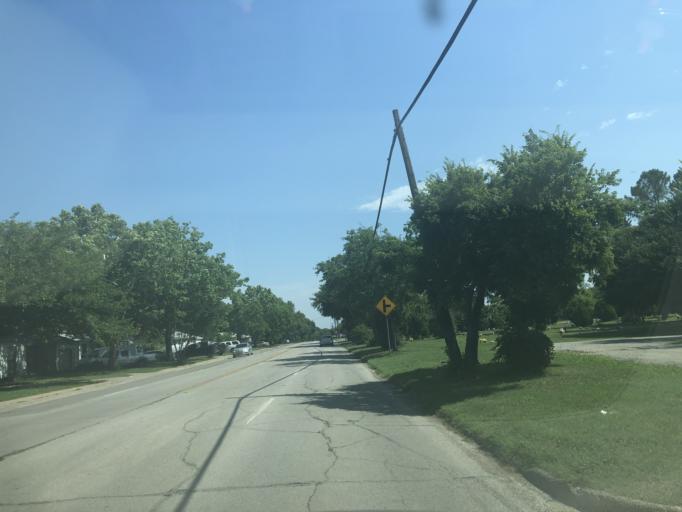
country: US
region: Texas
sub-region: Dallas County
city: Grand Prairie
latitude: 32.7308
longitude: -97.0059
